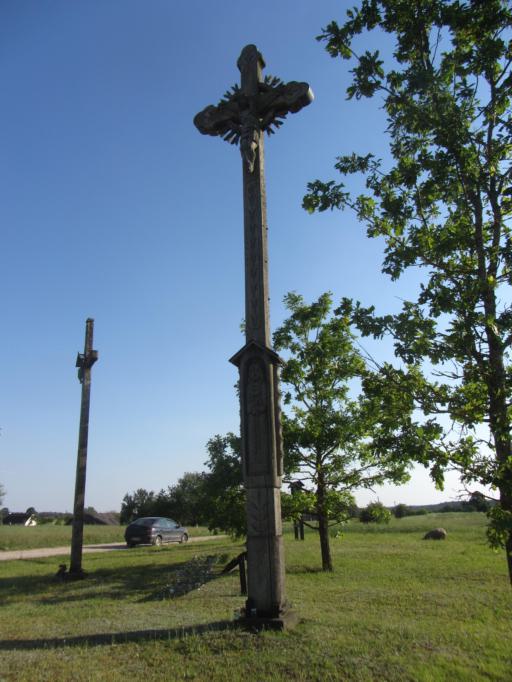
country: LT
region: Alytaus apskritis
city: Druskininkai
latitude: 54.2035
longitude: 24.0005
